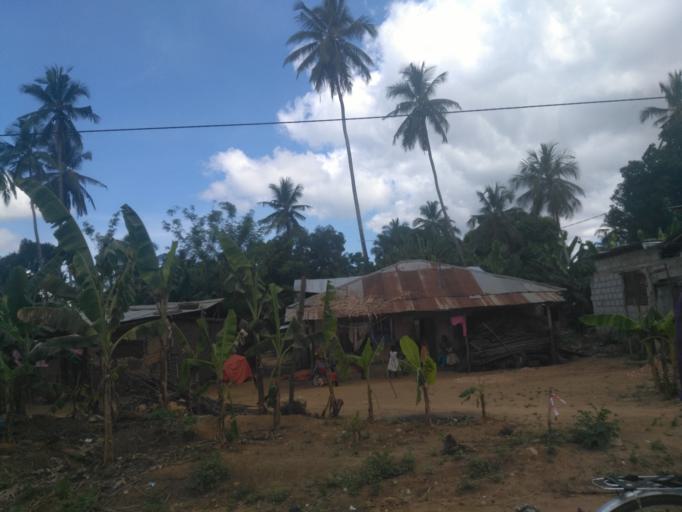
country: TZ
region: Zanzibar North
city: Gamba
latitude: -5.9733
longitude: 39.3021
